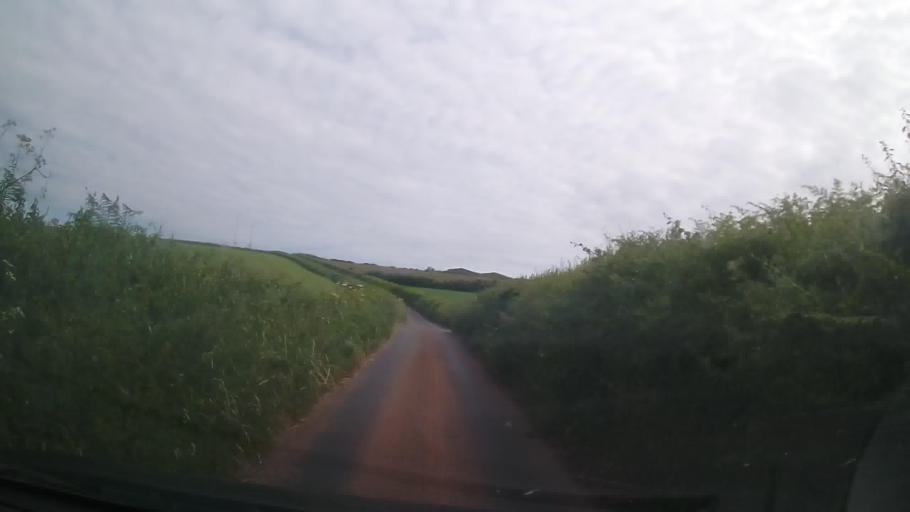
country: GB
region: England
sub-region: Devon
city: Salcombe
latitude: 50.2364
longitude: -3.6742
